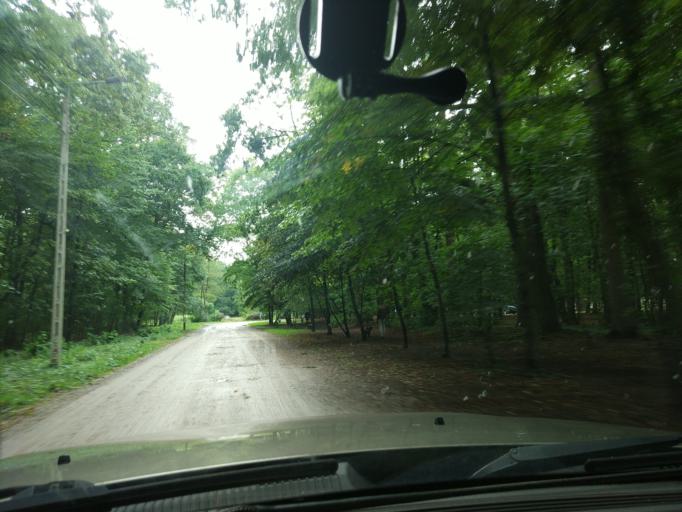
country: PL
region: Masovian Voivodeship
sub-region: Powiat grodziski
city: Podkowa Lesna
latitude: 52.1202
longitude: 20.7208
